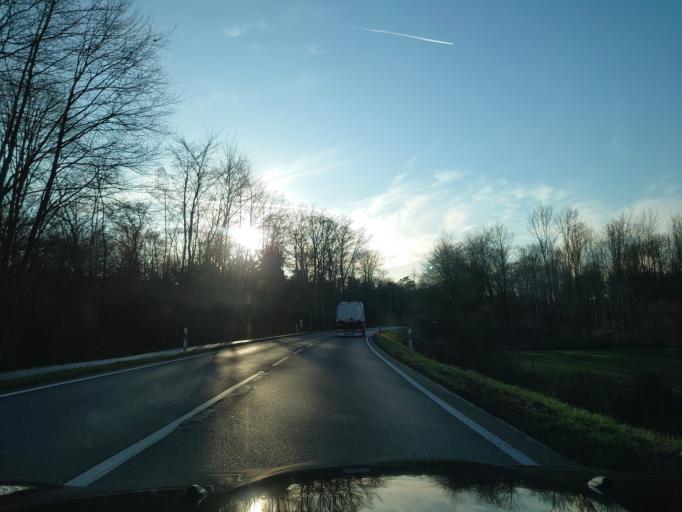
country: DE
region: North Rhine-Westphalia
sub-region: Regierungsbezirk Dusseldorf
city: Dormagen
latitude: 51.0740
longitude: 6.7582
